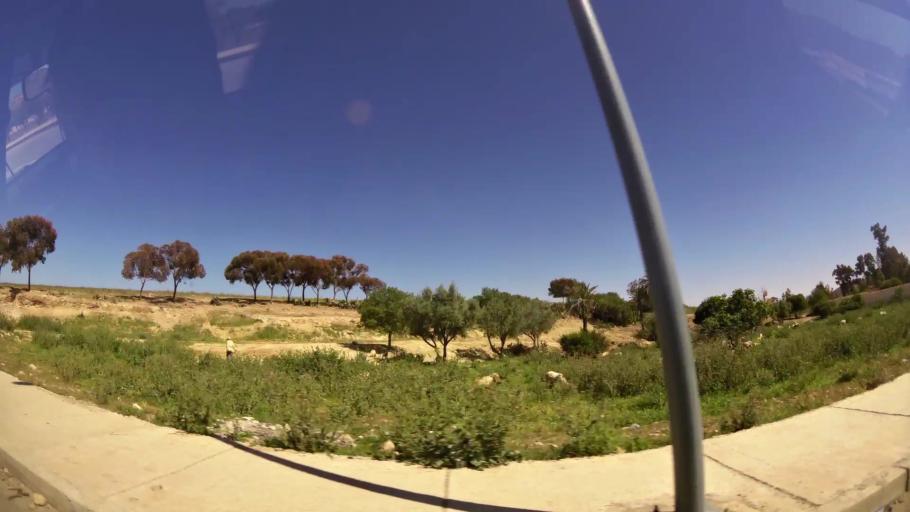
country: MA
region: Oriental
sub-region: Oujda-Angad
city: Oujda
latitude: 34.6682
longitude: -1.8619
